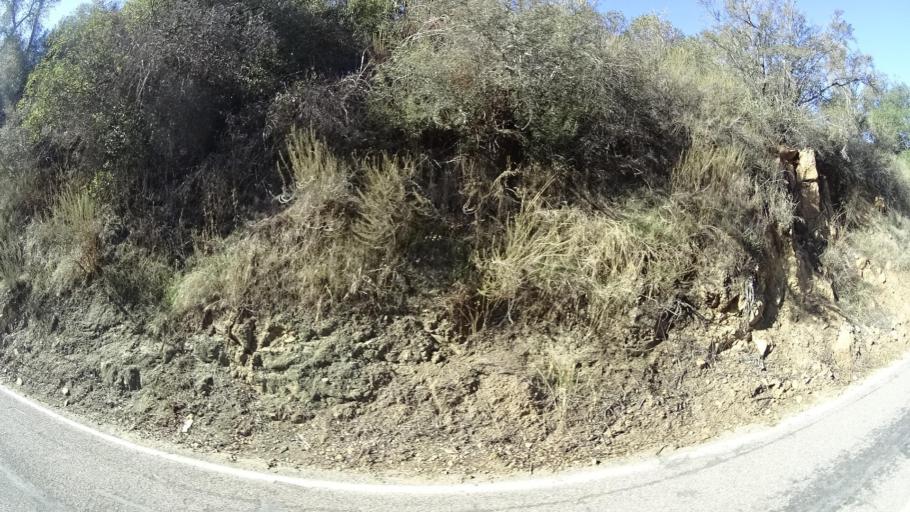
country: US
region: California
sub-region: San Diego County
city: Jamul
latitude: 32.7099
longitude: -116.7793
